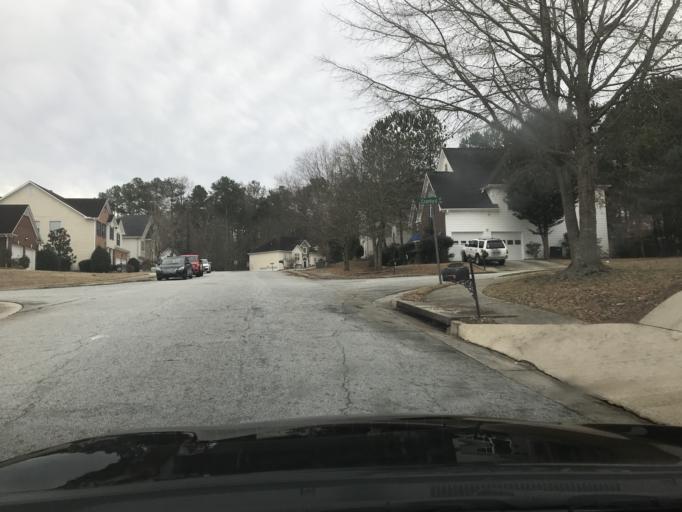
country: US
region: Georgia
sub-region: Fulton County
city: East Point
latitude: 33.7134
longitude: -84.5046
